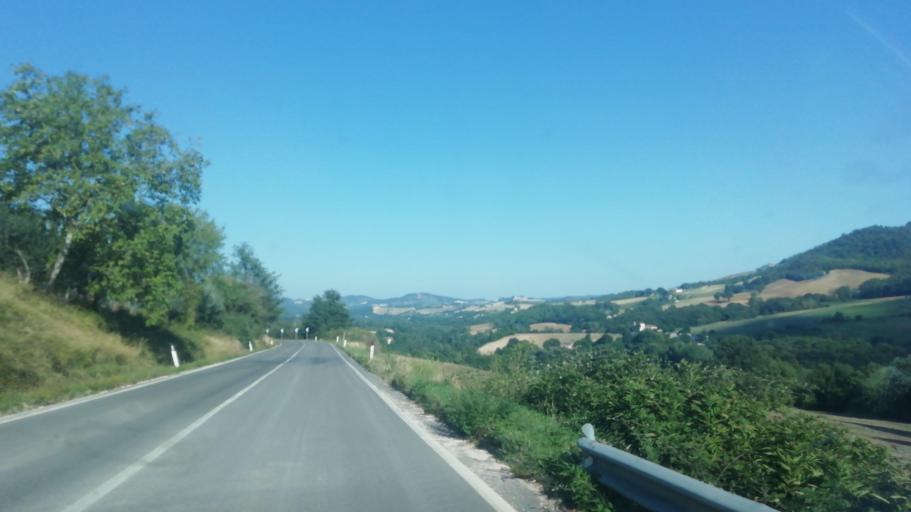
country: IT
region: The Marches
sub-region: Provincia di Pesaro e Urbino
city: Frontone
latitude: 43.5415
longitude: 12.7566
